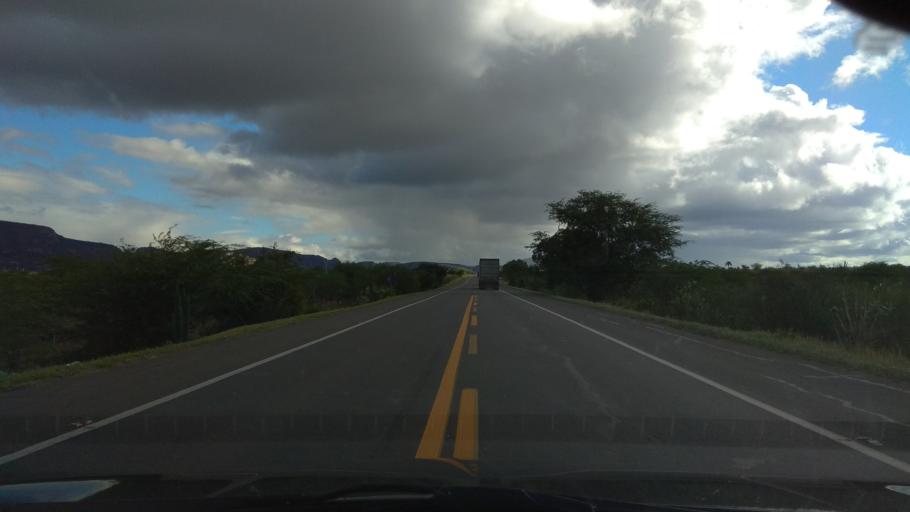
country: BR
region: Bahia
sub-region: Castro Alves
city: Castro Alves
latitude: -12.6993
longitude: -39.7099
